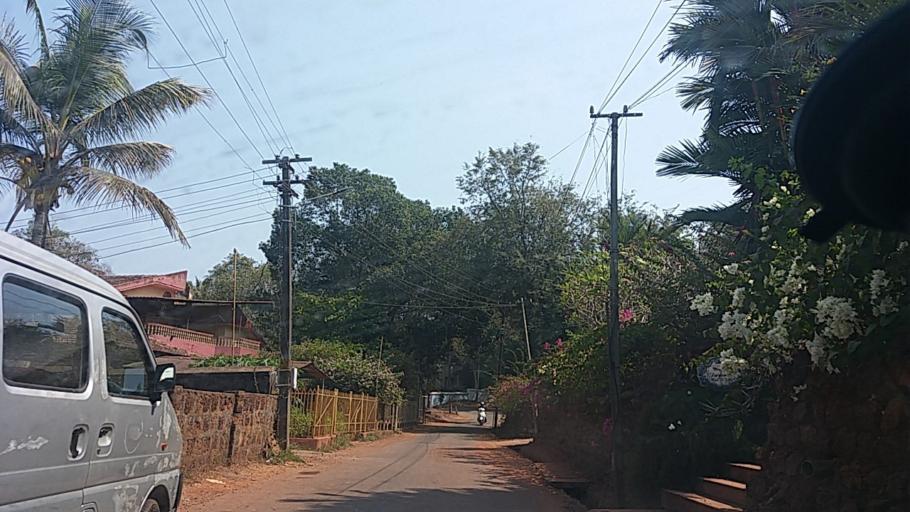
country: IN
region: Goa
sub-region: North Goa
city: Saligao
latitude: 15.5387
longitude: 73.7847
